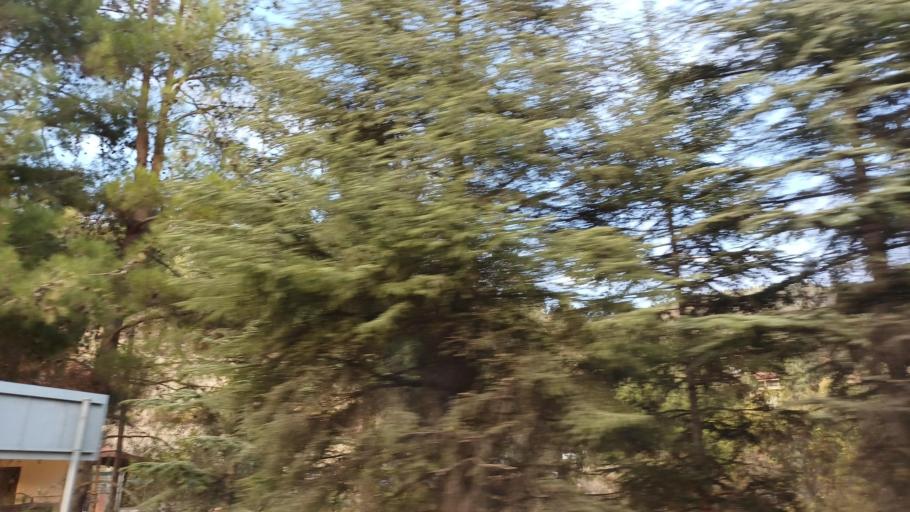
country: CY
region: Lefkosia
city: Kakopetria
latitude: 34.9823
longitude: 32.9073
